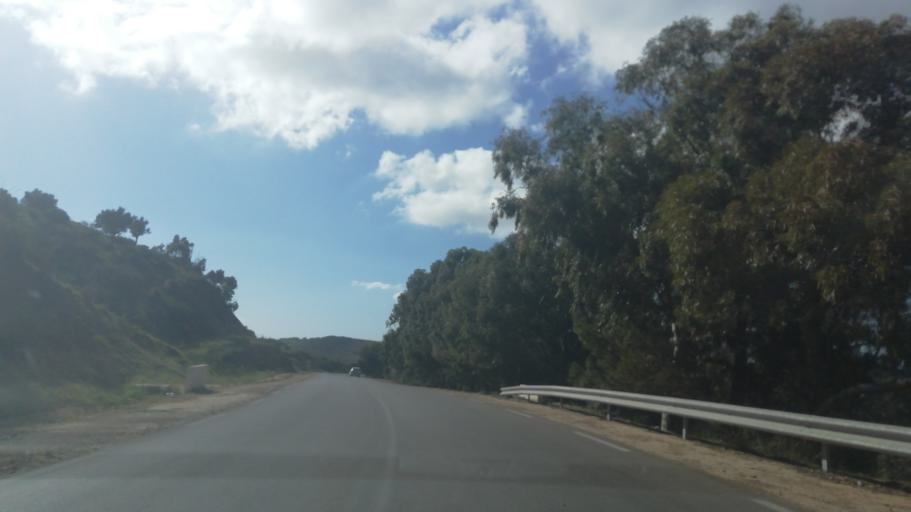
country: DZ
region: Relizane
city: Relizane
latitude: 36.0904
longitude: 0.4725
